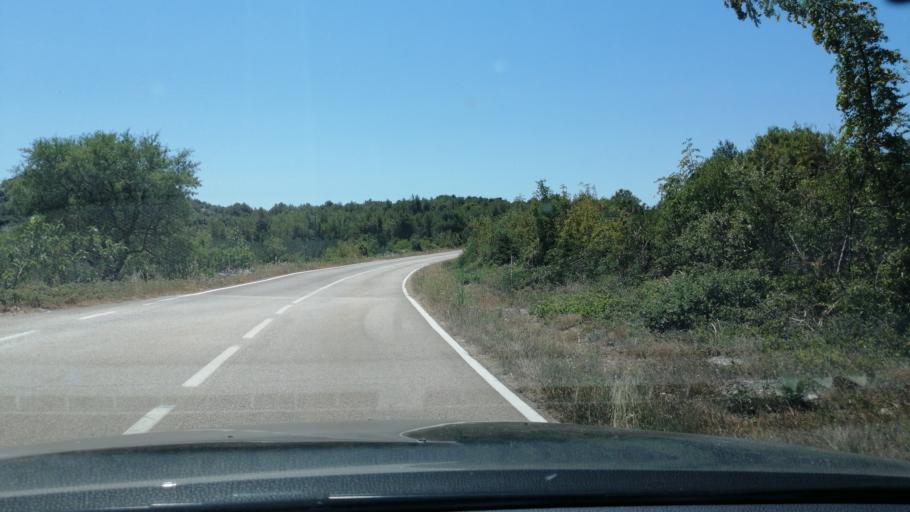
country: HR
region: Sibensko-Kniniska
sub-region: Grad Sibenik
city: Pirovac
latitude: 43.8393
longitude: 15.6899
